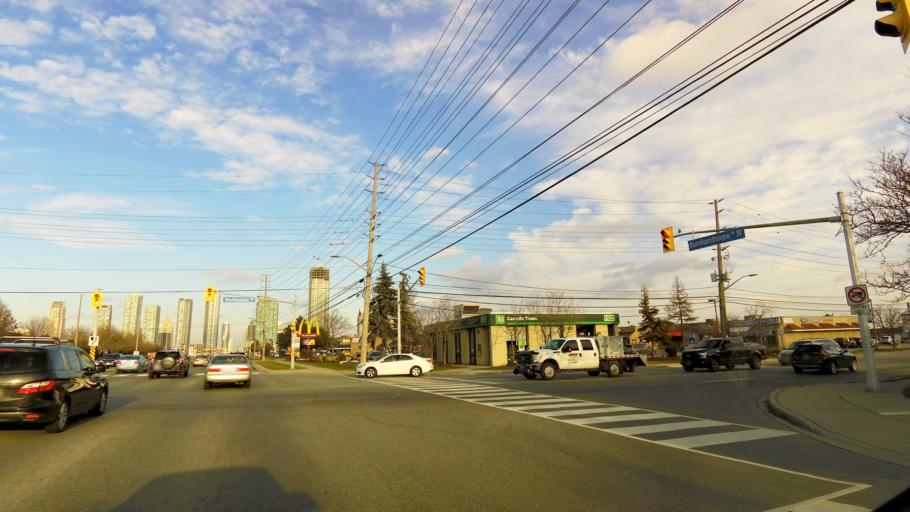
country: CA
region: Ontario
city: Mississauga
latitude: 43.5761
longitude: -79.6552
